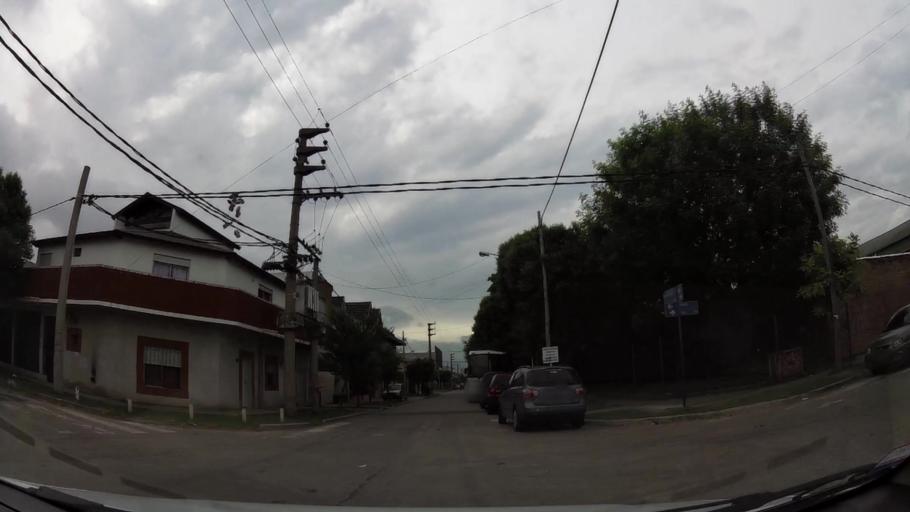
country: AR
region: Buenos Aires
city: San Justo
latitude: -34.6978
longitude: -58.5265
